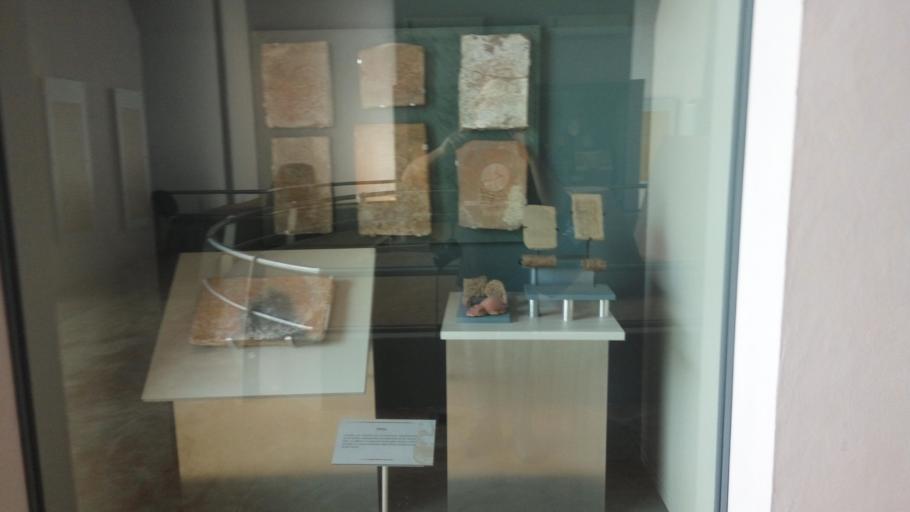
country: MX
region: Tabasco
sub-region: Comalcalco
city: Oriente 1ra. Seccion (Santo Domingo)
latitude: 18.2808
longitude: -93.2051
